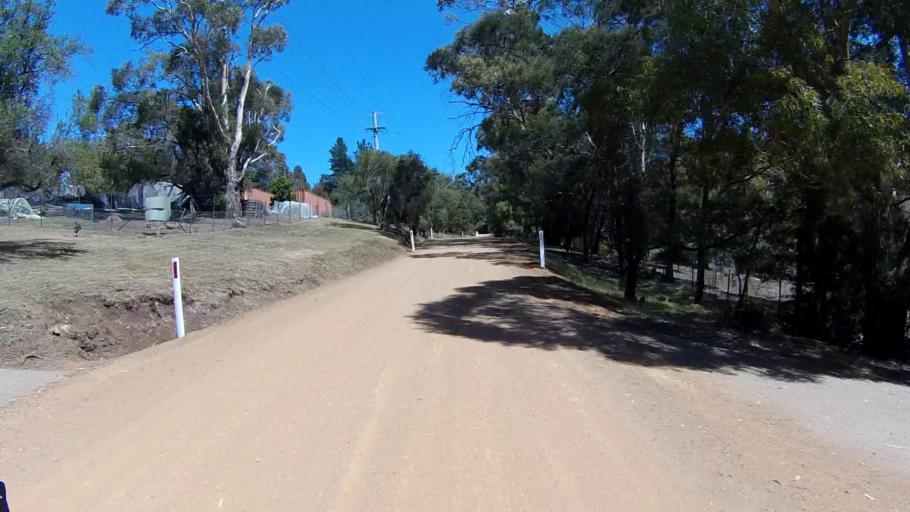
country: AU
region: Tasmania
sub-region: Clarence
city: Cambridge
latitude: -42.8516
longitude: 147.4367
